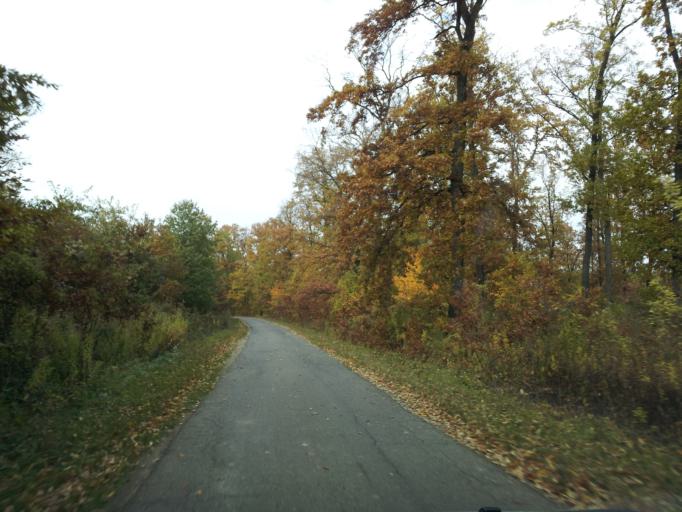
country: HU
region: Gyor-Moson-Sopron
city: Pannonhalma
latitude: 47.4912
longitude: 17.7346
